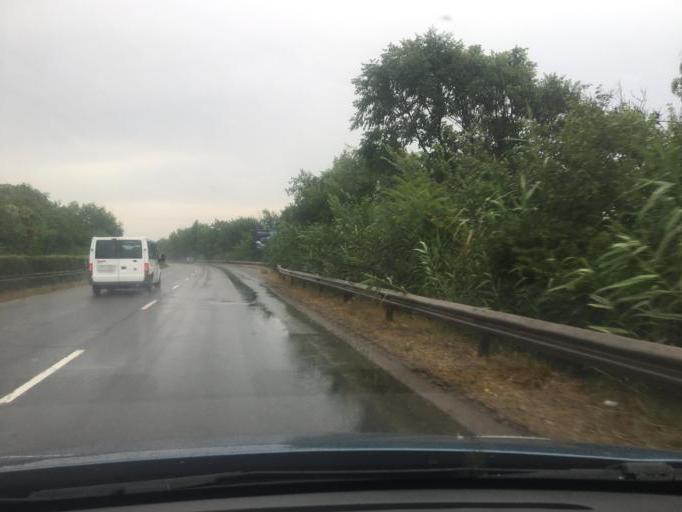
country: BG
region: Burgas
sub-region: Obshtina Burgas
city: Burgas
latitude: 42.5347
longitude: 27.4708
